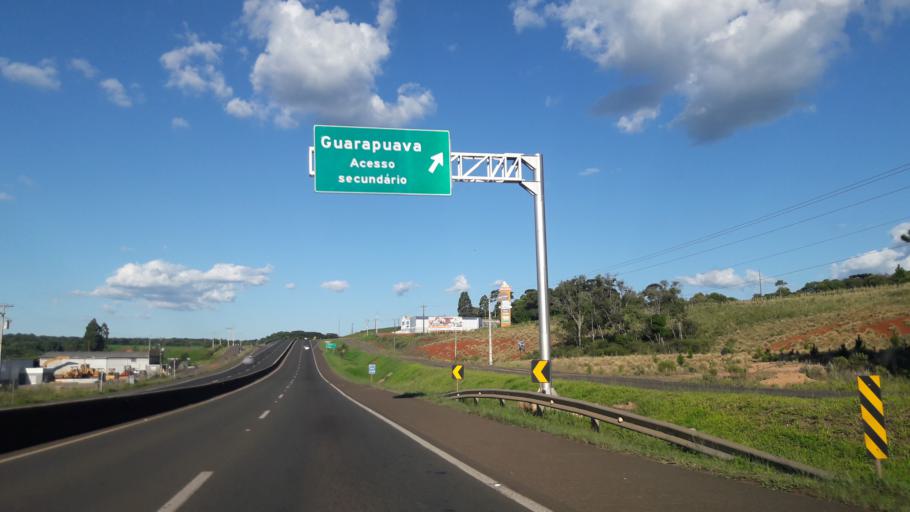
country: BR
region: Parana
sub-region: Guarapuava
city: Guarapuava
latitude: -25.3425
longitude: -51.4346
